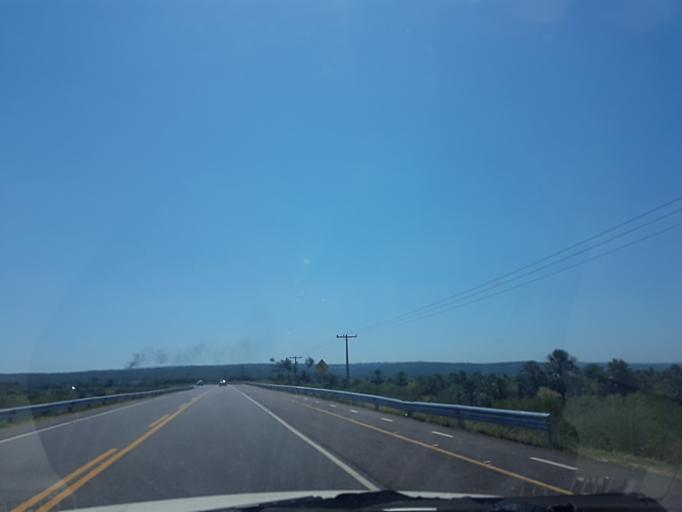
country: PY
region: Cordillera
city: Emboscada
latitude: -25.2076
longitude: -57.3775
